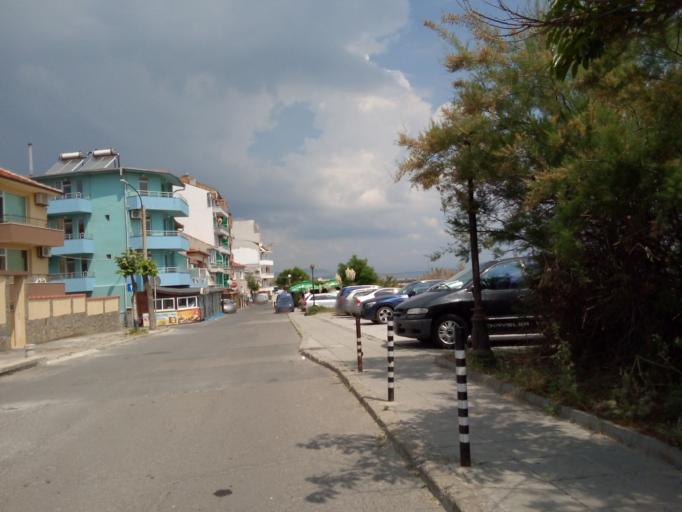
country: BG
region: Burgas
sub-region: Obshtina Pomorie
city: Pomorie
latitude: 42.5580
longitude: 27.6466
